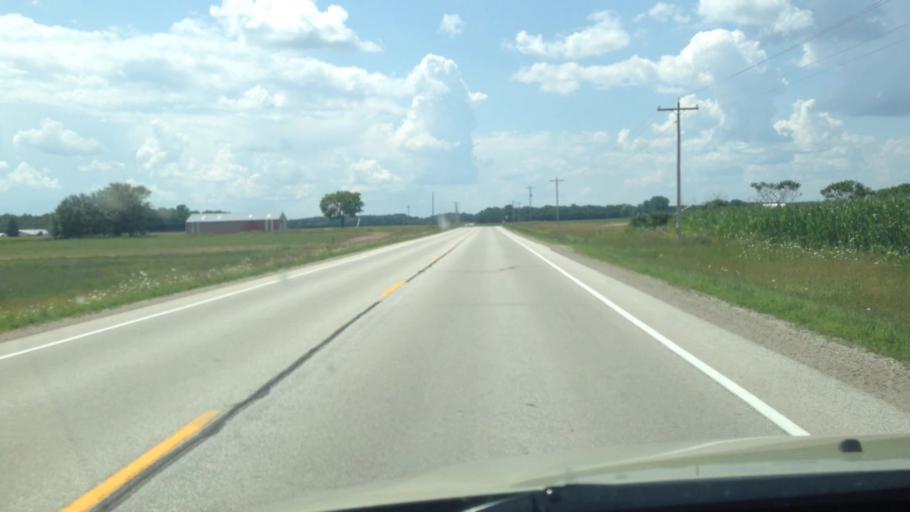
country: US
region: Wisconsin
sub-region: Brown County
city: Pulaski
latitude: 44.6463
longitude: -88.1543
